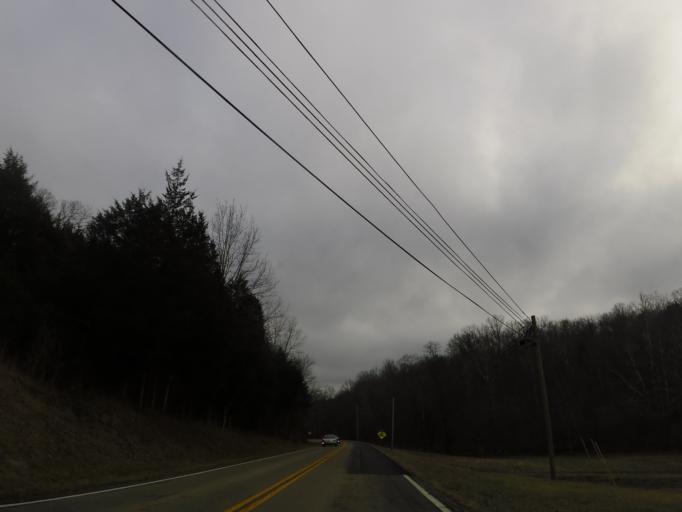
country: US
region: Kentucky
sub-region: Trimble County
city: Bedford
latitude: 38.5732
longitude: -85.2979
